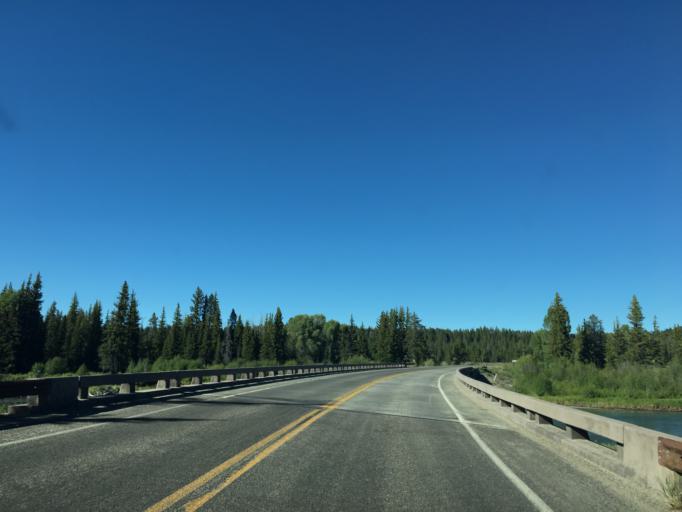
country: US
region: Wyoming
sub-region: Teton County
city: Jackson
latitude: 43.8379
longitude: -110.5131
